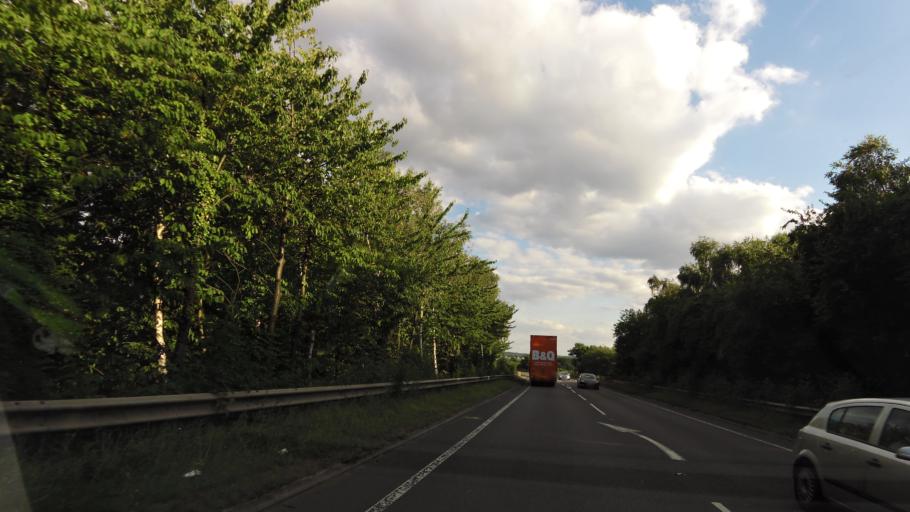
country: GB
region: England
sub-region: Nottinghamshire
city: Worksop
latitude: 53.3174
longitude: -1.1521
